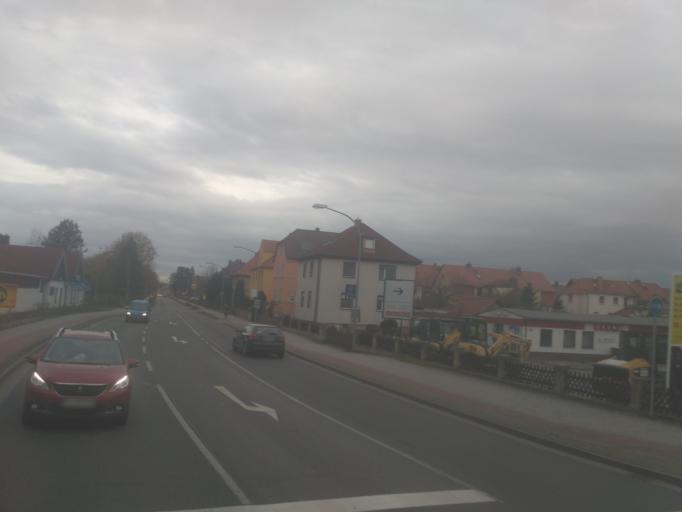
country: DE
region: Brandenburg
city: Elsterwerda
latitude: 51.4647
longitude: 13.5291
